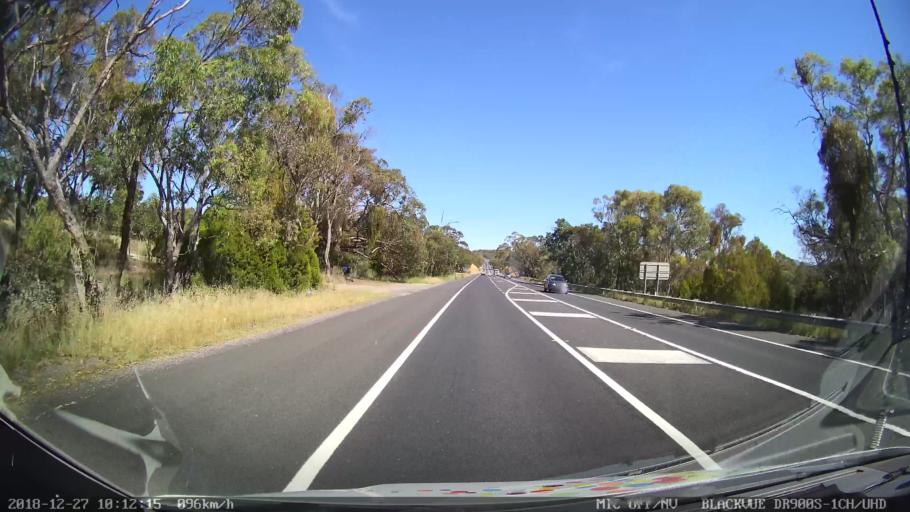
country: AU
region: New South Wales
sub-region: Bathurst Regional
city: Kelso
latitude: -33.4451
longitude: 149.7626
